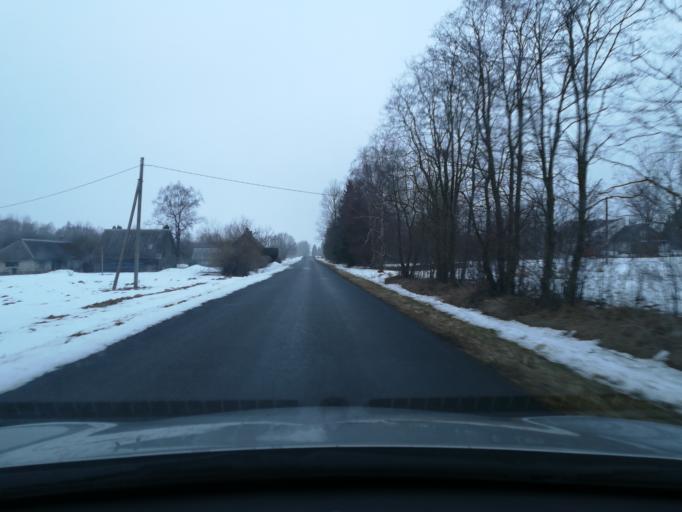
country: EE
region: Harju
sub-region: Raasiku vald
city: Raasiku
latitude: 59.3430
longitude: 25.2243
